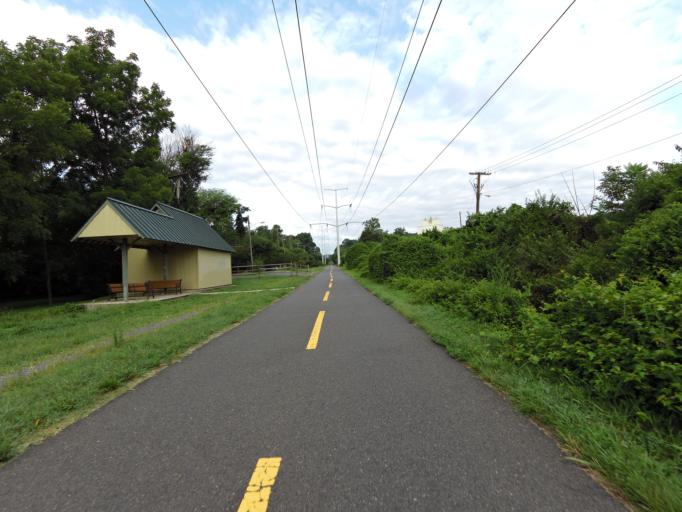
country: US
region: Virginia
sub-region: City of Falls Church
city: Falls Church
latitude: 38.8918
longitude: -77.1893
